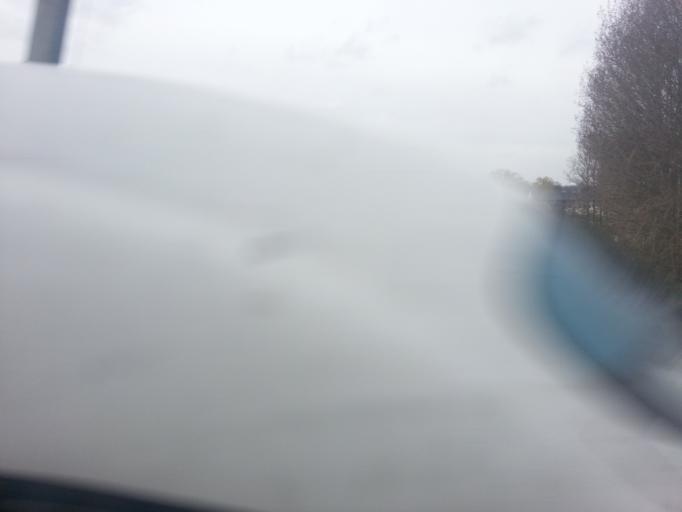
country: NL
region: Gelderland
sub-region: Gemeente Culemborg
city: Culemborg
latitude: 51.9673
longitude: 5.2070
